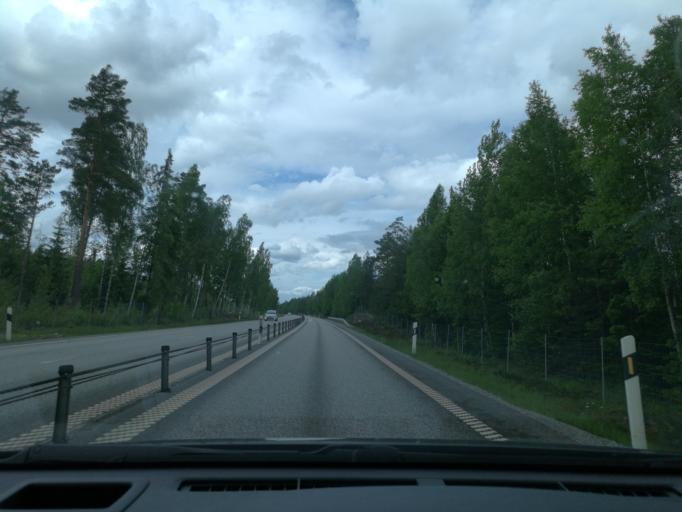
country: SE
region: Vaestmanland
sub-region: Surahammars Kommun
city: Surahammar
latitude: 59.7107
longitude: 16.2450
